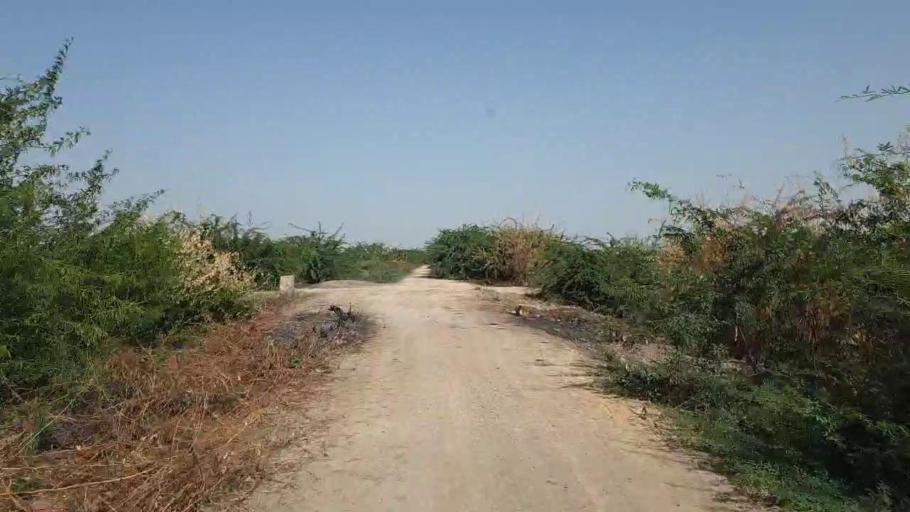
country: PK
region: Sindh
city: Tando Bago
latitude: 24.7195
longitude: 69.0730
